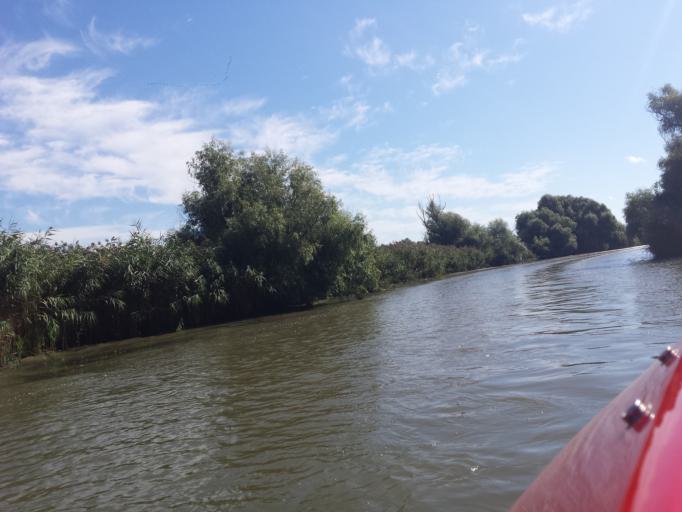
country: RO
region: Tulcea
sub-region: Comuna Pardina
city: Pardina
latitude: 45.2389
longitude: 29.0954
